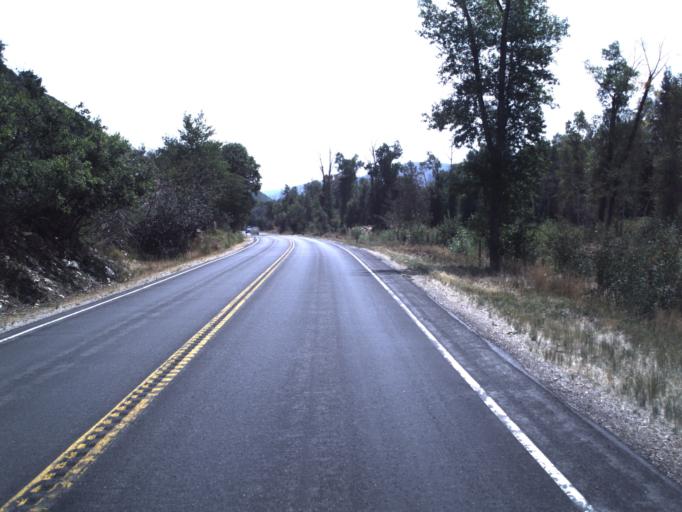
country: US
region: Utah
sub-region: Summit County
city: Francis
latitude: 40.5704
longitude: -111.2023
